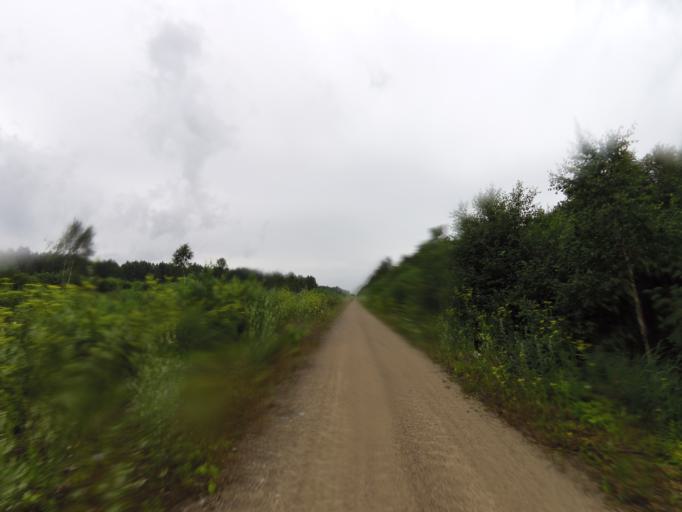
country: EE
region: Laeaene
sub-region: Ridala Parish
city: Uuemoisa
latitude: 58.9564
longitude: 23.8512
